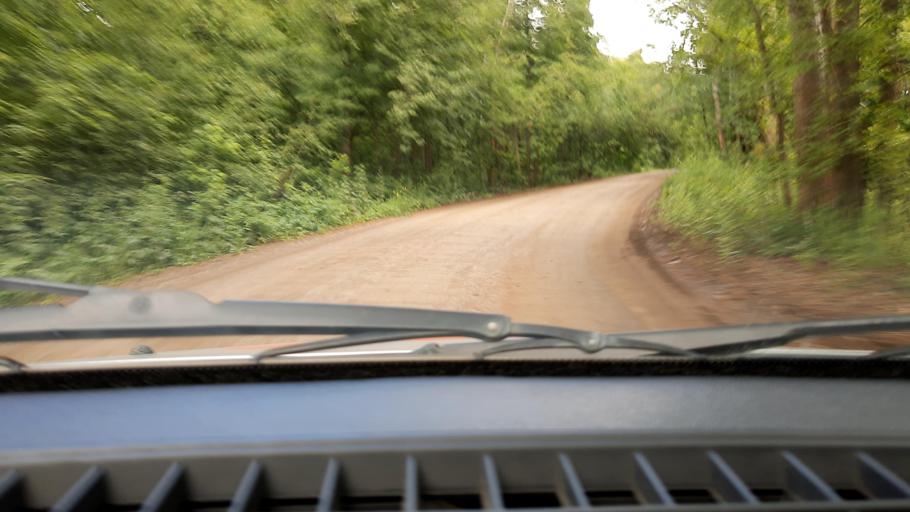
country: RU
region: Bashkortostan
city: Ufa
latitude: 54.6781
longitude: 56.0613
